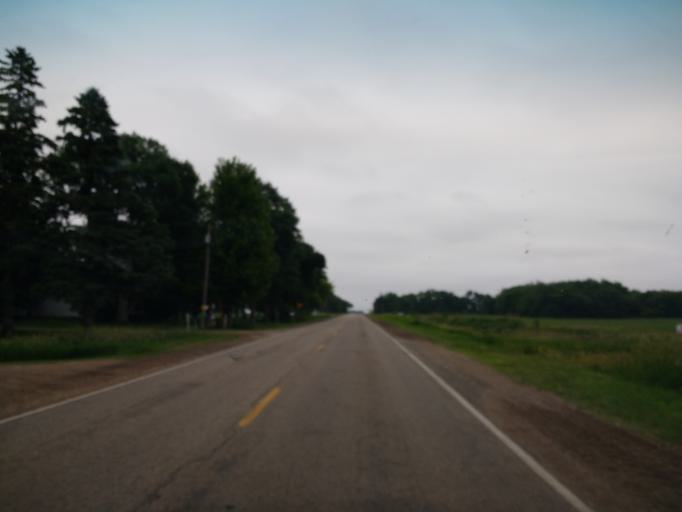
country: US
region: Iowa
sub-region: Dickinson County
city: Milford
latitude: 43.3279
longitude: -95.1175
